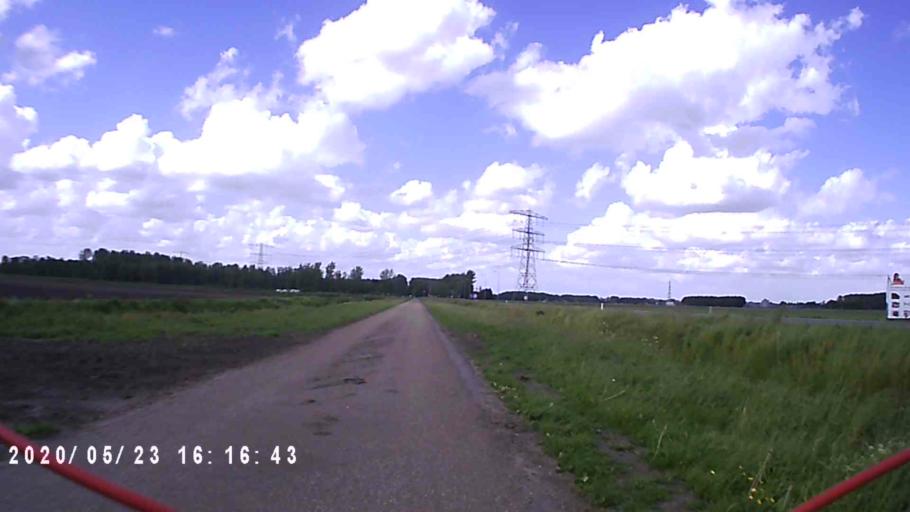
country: NL
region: Groningen
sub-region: Gemeente Appingedam
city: Appingedam
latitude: 53.2633
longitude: 6.8750
